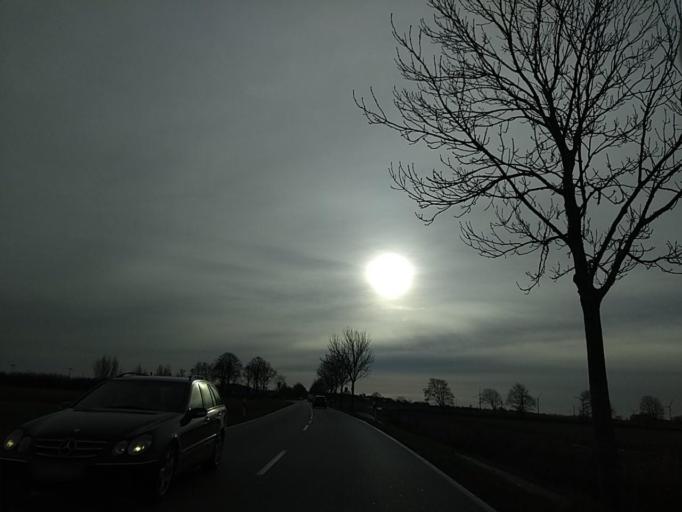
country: DE
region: Lower Saxony
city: Jemgum
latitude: 53.2582
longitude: 7.3847
